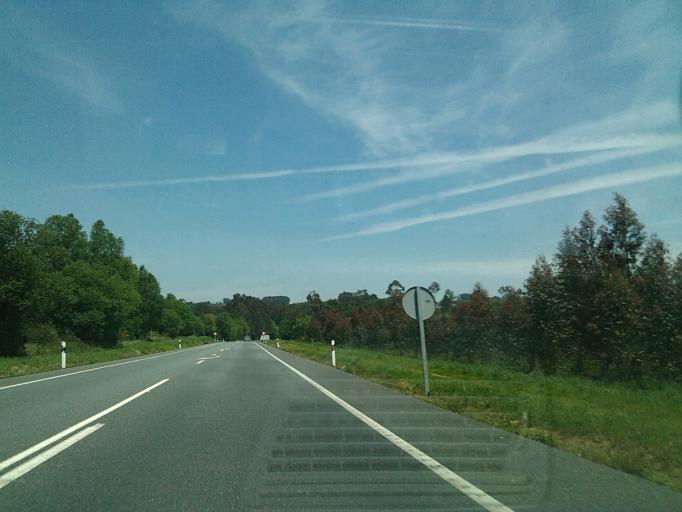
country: ES
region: Galicia
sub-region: Provincia da Coruna
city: Mesia
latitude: 43.0807
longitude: -8.1932
